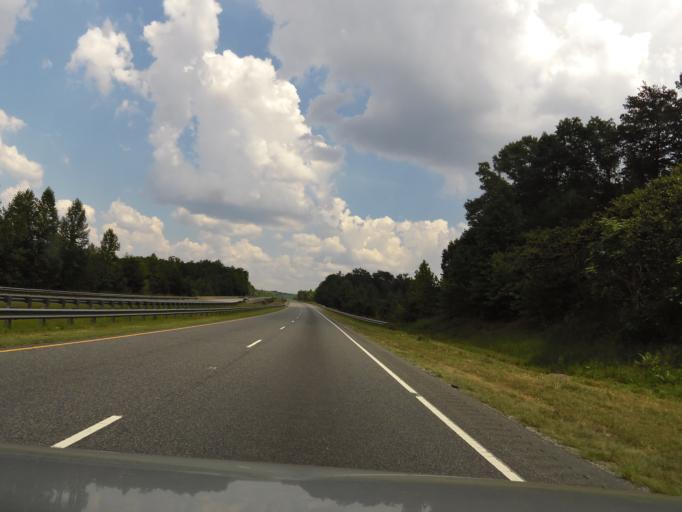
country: US
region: North Carolina
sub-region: Rutherford County
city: Rutherfordton
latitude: 35.2971
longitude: -81.9712
